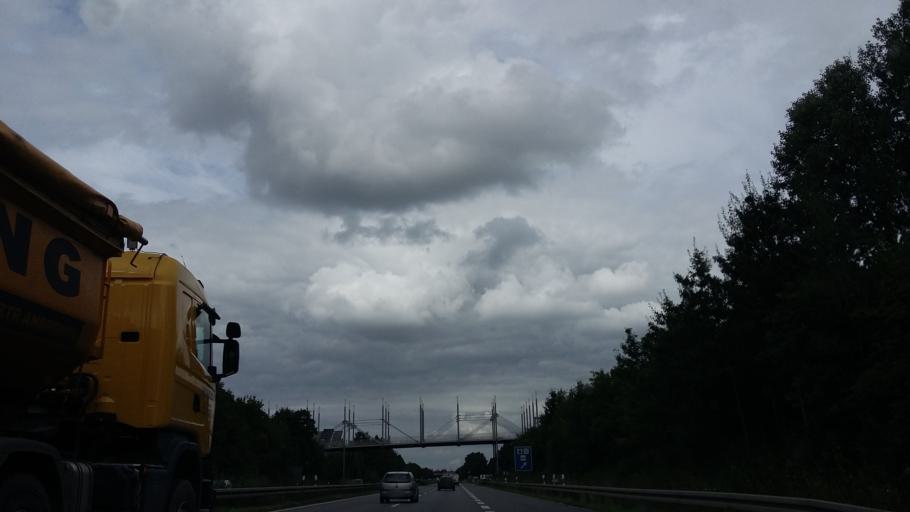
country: DE
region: Lower Saxony
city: Laatzen
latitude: 52.3200
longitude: 9.8134
